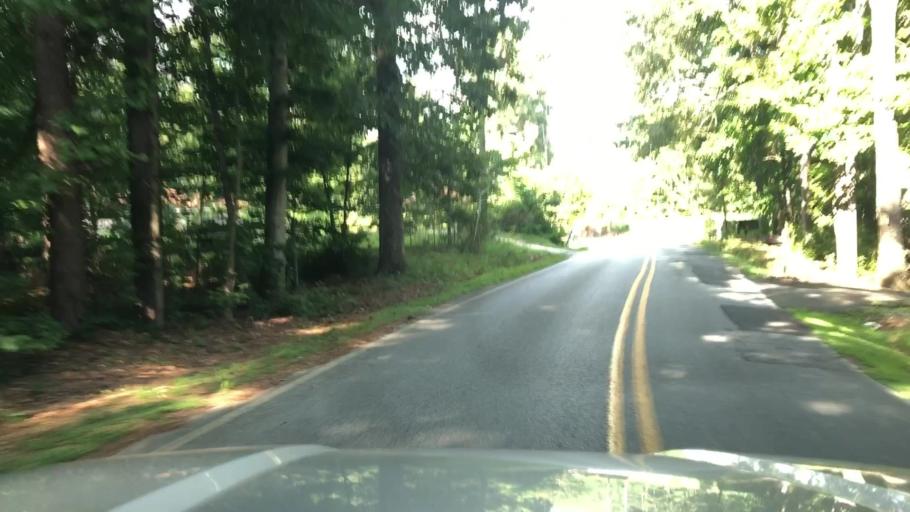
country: US
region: Georgia
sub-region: Paulding County
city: Dallas
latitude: 33.9905
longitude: -84.8682
